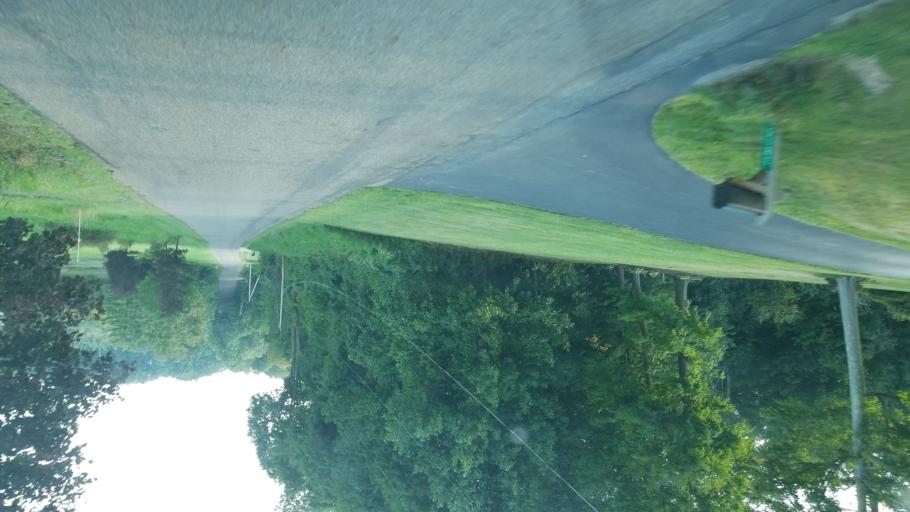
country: US
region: Ohio
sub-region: Sandusky County
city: Bellville
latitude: 40.6543
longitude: -82.5013
